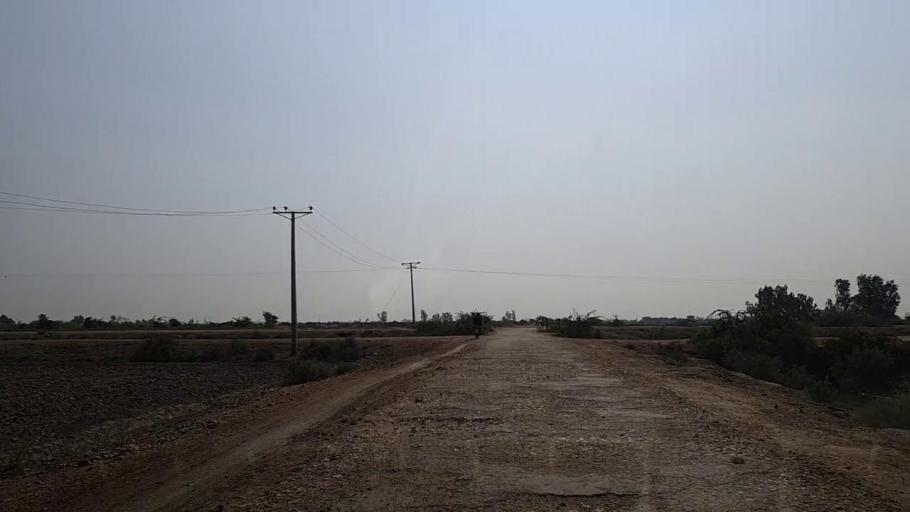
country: PK
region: Sindh
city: Thatta
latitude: 24.7120
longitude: 67.7685
